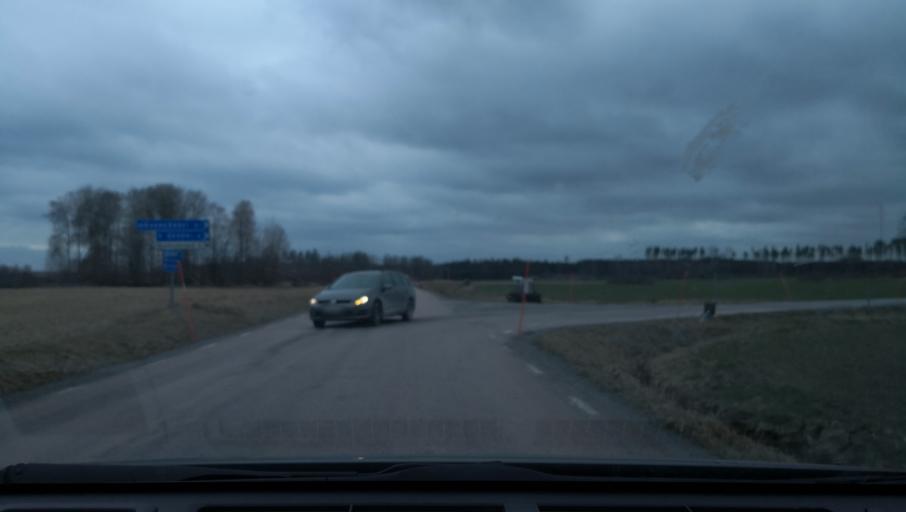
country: SE
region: Vaestmanland
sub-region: Kopings Kommun
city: Kolsva
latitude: 59.5612
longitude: 15.7413
